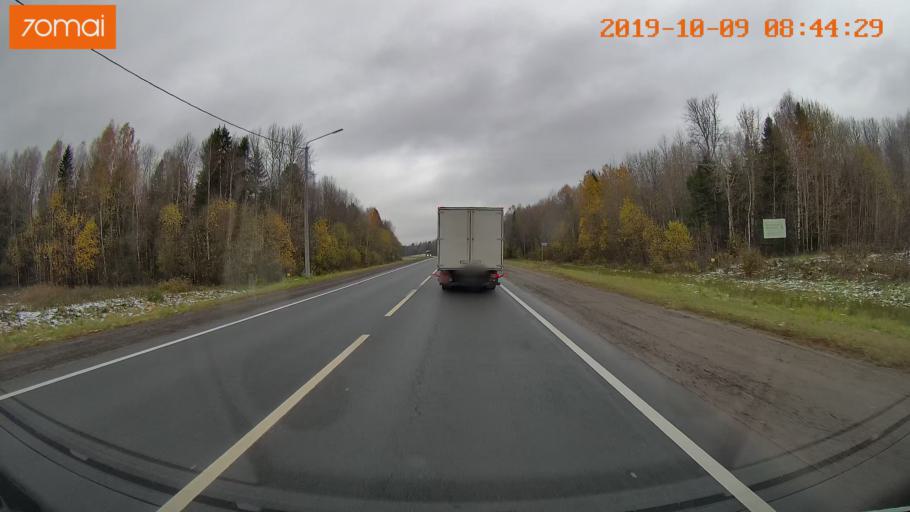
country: RU
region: Vologda
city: Gryazovets
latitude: 59.0372
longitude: 40.1074
